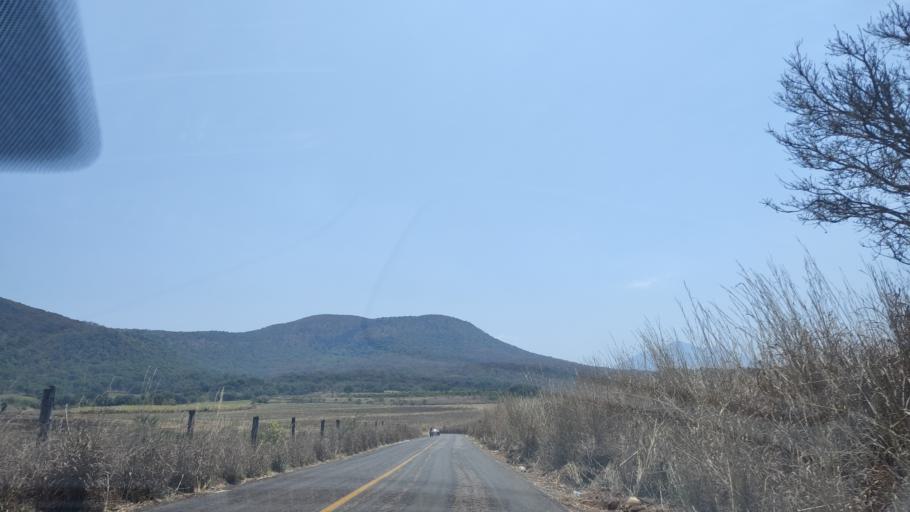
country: MX
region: Nayarit
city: Puga
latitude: 21.5750
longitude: -104.7573
